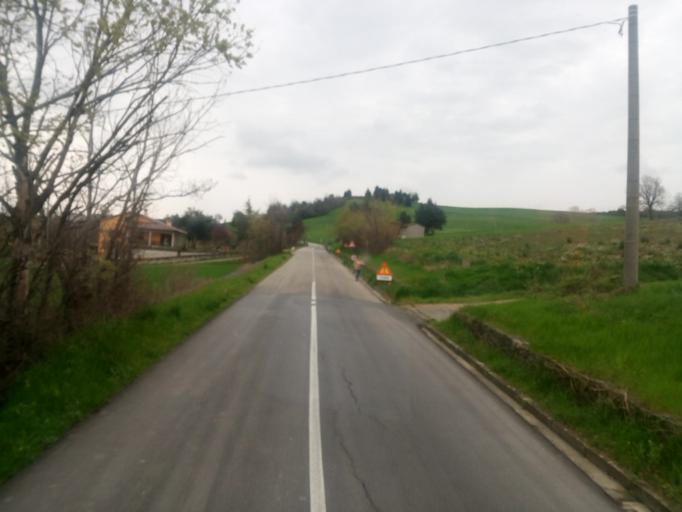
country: IT
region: Emilia-Romagna
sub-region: Forli-Cesena
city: Meldola
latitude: 44.1240
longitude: 12.0740
